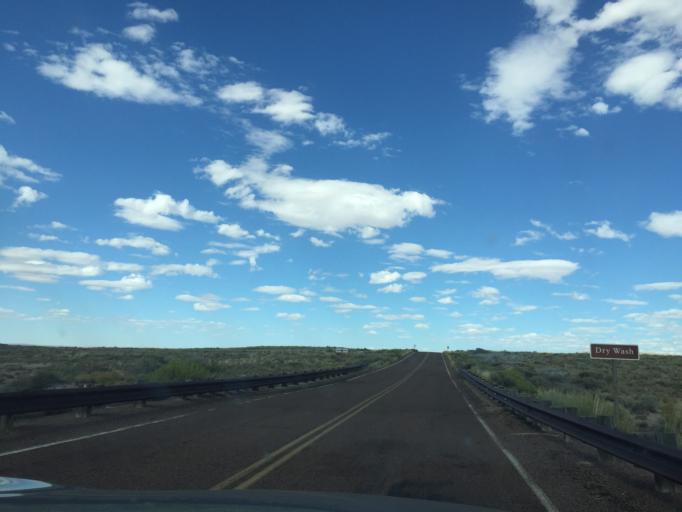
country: US
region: Arizona
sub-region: Navajo County
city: Holbrook
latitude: 34.8398
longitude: -109.8082
